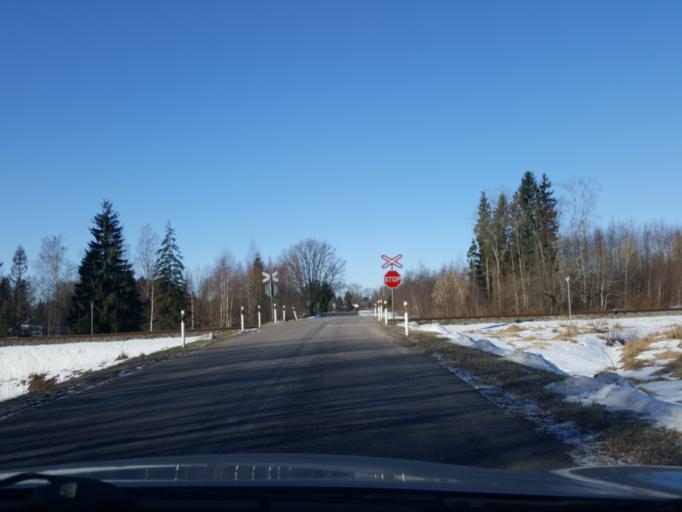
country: EE
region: Viljandimaa
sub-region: Suure-Jaani vald
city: Suure-Jaani
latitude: 58.5370
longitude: 25.5452
